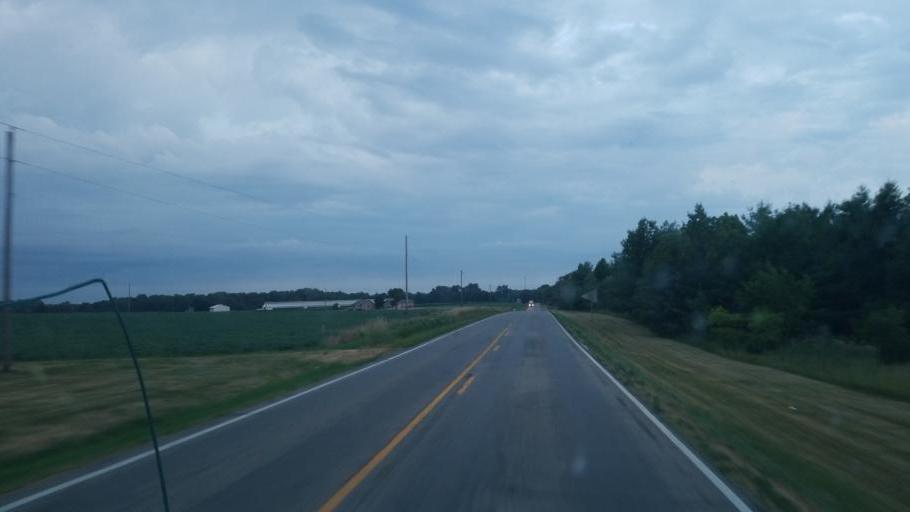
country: US
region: Ohio
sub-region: Defiance County
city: Hicksville
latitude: 41.3396
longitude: -84.8275
